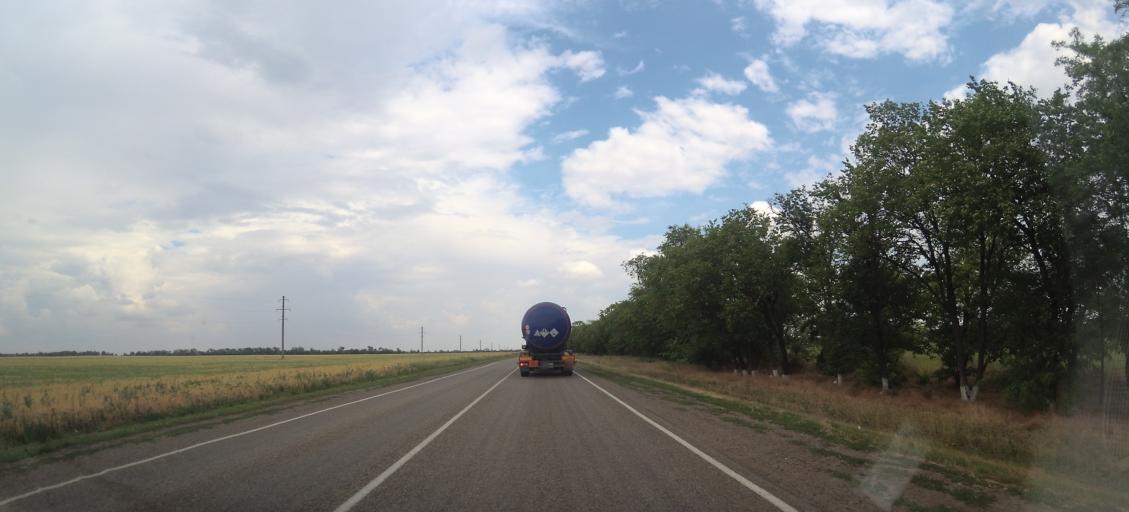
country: RU
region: Rostov
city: Peschanokopskoye
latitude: 46.2483
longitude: 41.2775
